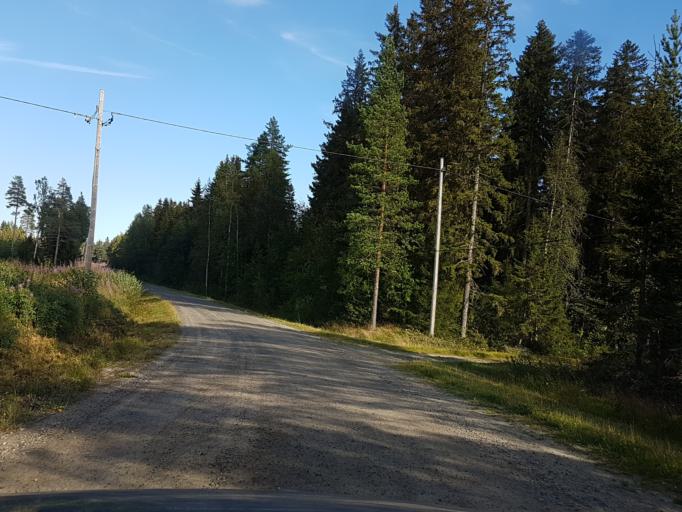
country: SE
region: Vaesterbotten
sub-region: Robertsfors Kommun
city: Robertsfors
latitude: 64.0495
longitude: 20.8742
